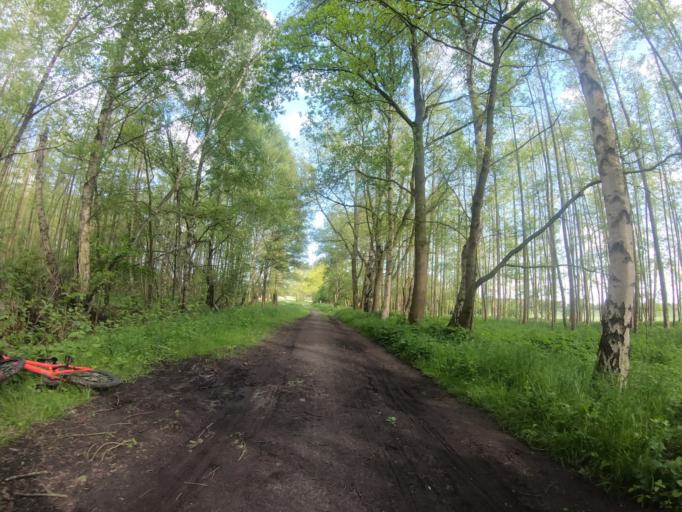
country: DE
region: Lower Saxony
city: Sassenburg
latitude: 52.5104
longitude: 10.6158
